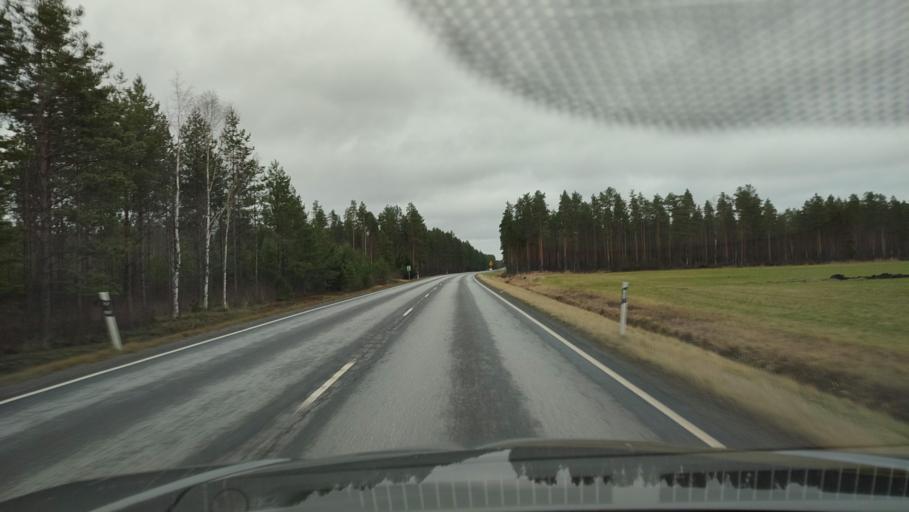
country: FI
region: Southern Ostrobothnia
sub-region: Seinaejoki
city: Kurikka
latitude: 62.5142
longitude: 22.3122
